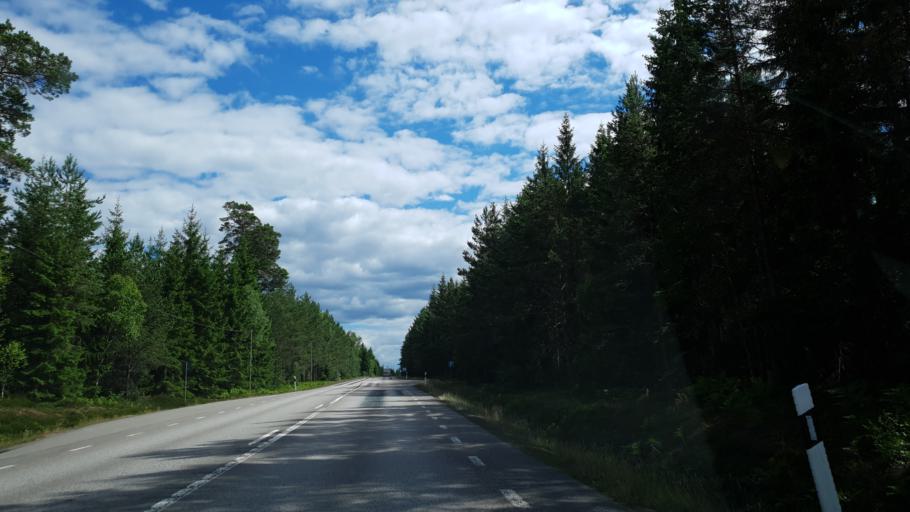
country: SE
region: Kronoberg
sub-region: Uppvidinge Kommun
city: Lenhovda
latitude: 56.8782
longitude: 15.3806
